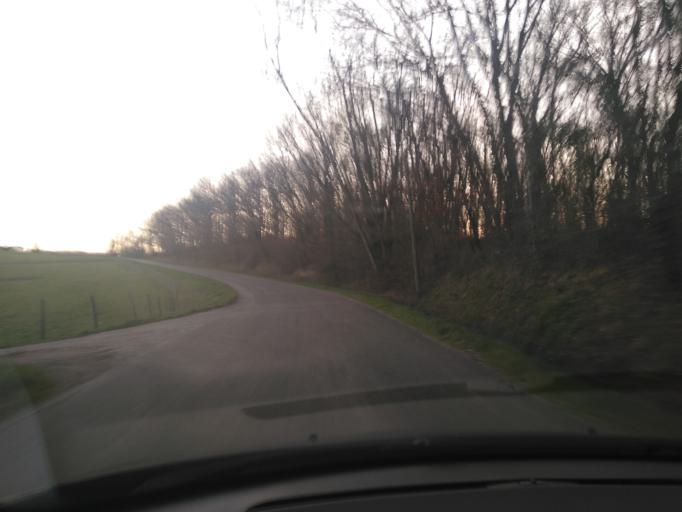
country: FR
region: Aquitaine
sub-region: Departement du Lot-et-Garonne
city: Saint-Hilaire
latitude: 44.5262
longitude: 0.6887
